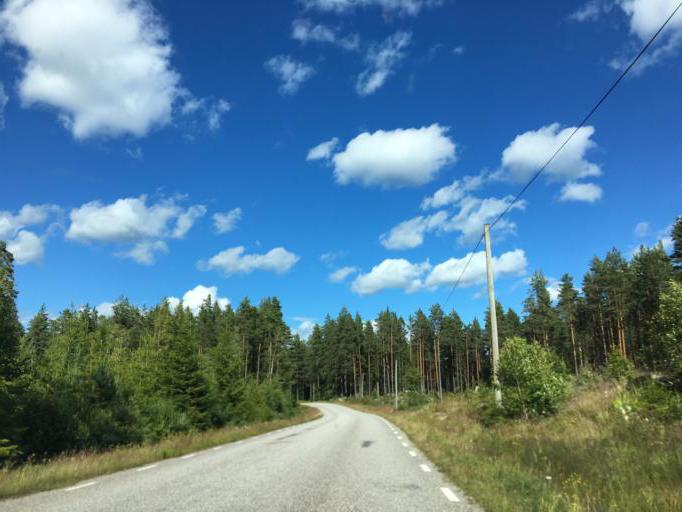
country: SE
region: OErebro
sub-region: Laxa Kommun
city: Laxa
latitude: 58.8160
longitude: 14.6730
